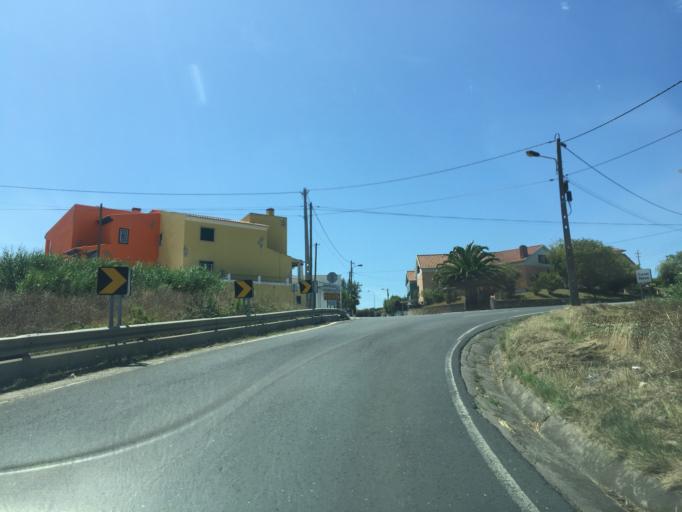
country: PT
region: Lisbon
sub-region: Lourinha
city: Lourinha
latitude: 39.2249
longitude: -9.3136
